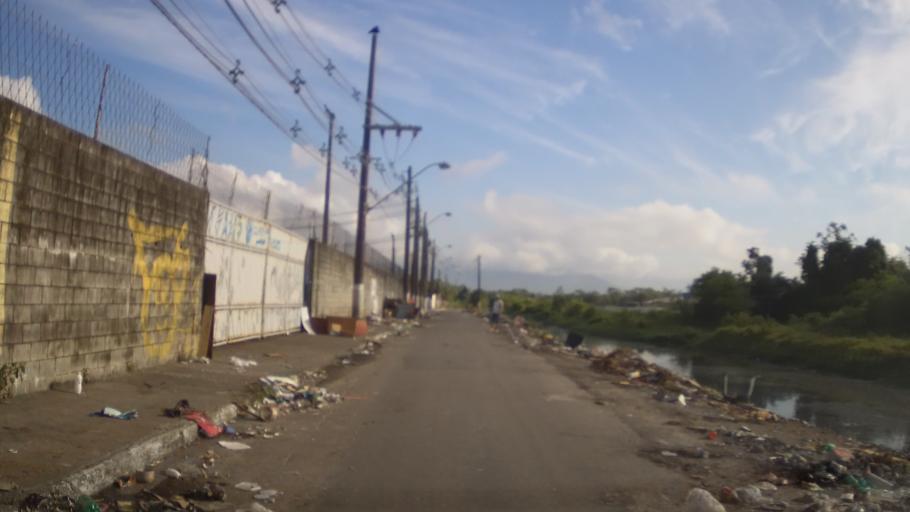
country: BR
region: Sao Paulo
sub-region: Praia Grande
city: Praia Grande
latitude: -24.0144
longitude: -46.4752
